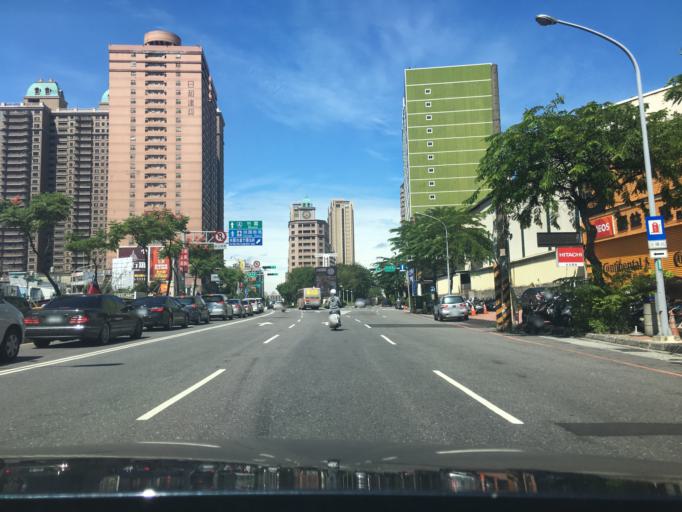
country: TW
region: Taiwan
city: Taoyuan City
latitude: 25.0406
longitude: 121.2961
